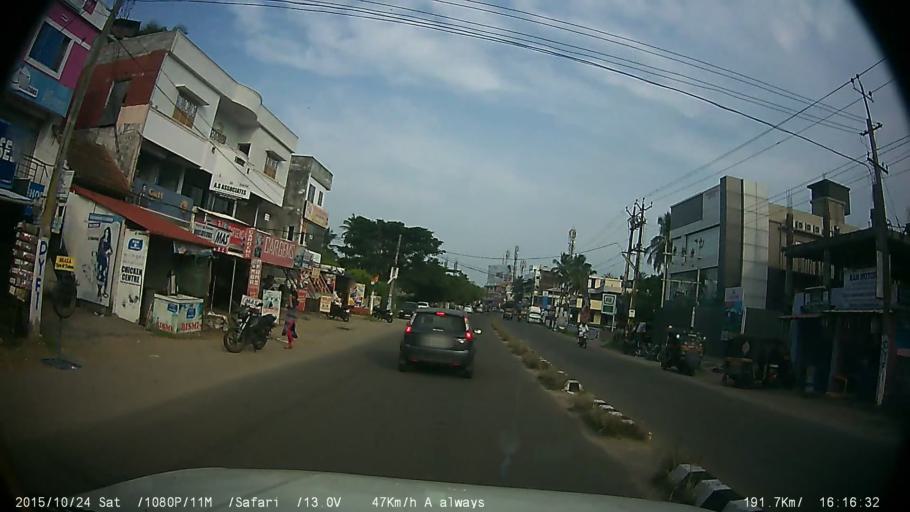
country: IN
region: Kerala
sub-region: Palakkad district
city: Palakkad
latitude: 10.7729
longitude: 76.6694
